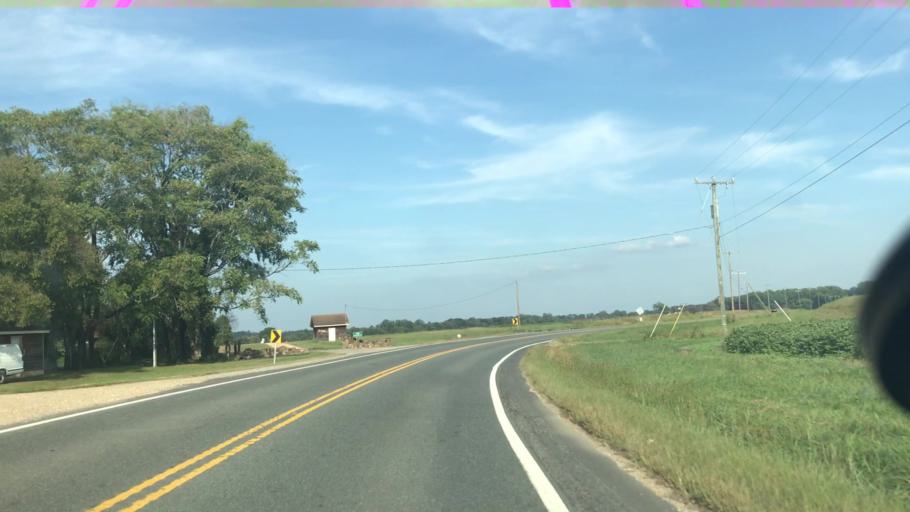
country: US
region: Virginia
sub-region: City of Fredericksburg
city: Fredericksburg
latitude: 38.2382
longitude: -77.3950
